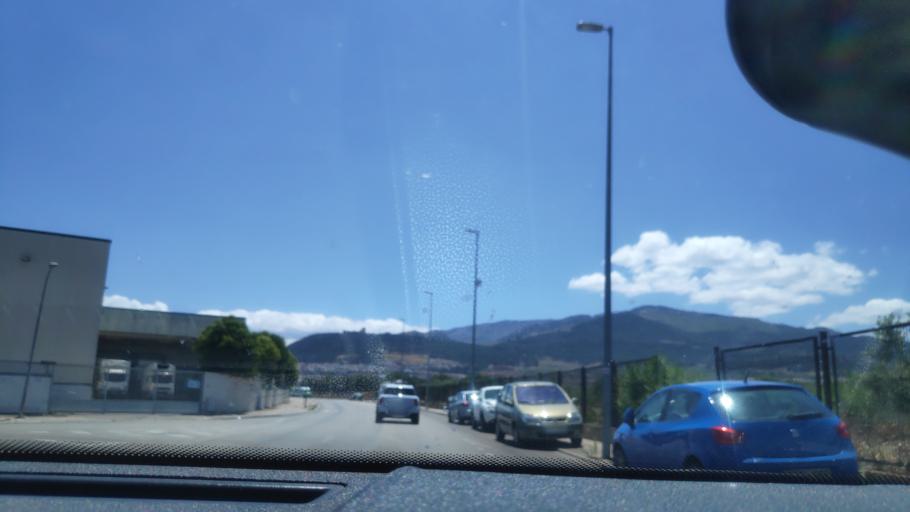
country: ES
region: Andalusia
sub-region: Provincia de Jaen
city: Jaen
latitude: 37.7978
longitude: -3.7928
